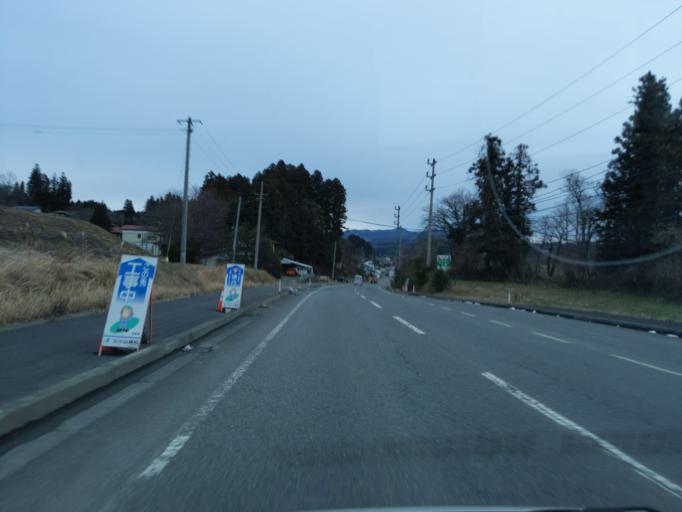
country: JP
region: Iwate
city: Ichinoseki
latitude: 39.0232
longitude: 141.3240
